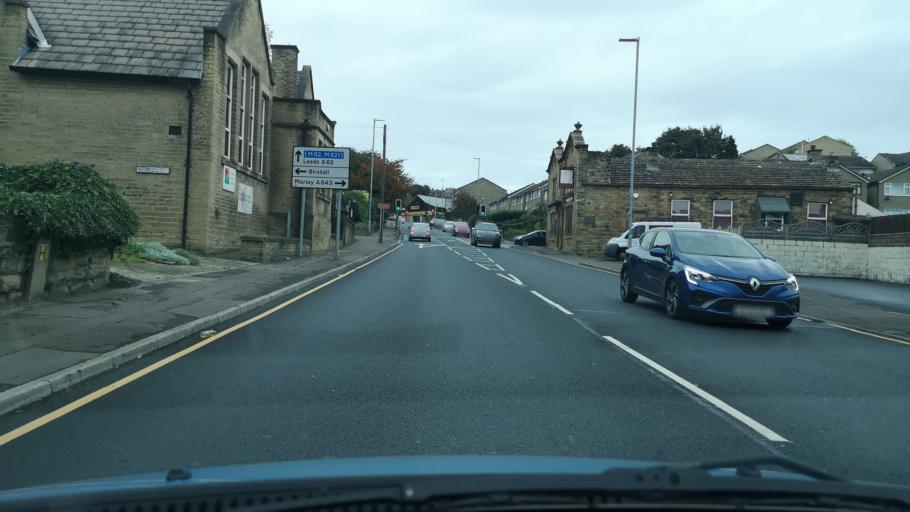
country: GB
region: England
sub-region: City and Borough of Leeds
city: Drighlington
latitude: 53.7305
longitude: -1.6595
